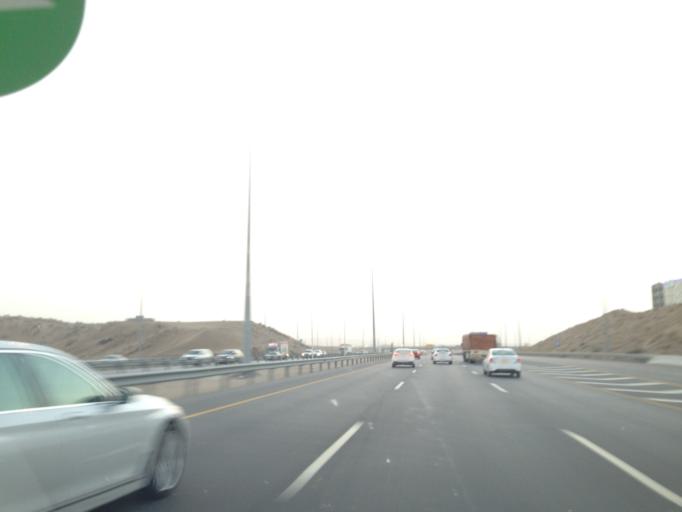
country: OM
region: Muhafazat Masqat
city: Bawshar
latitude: 23.5702
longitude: 58.4136
